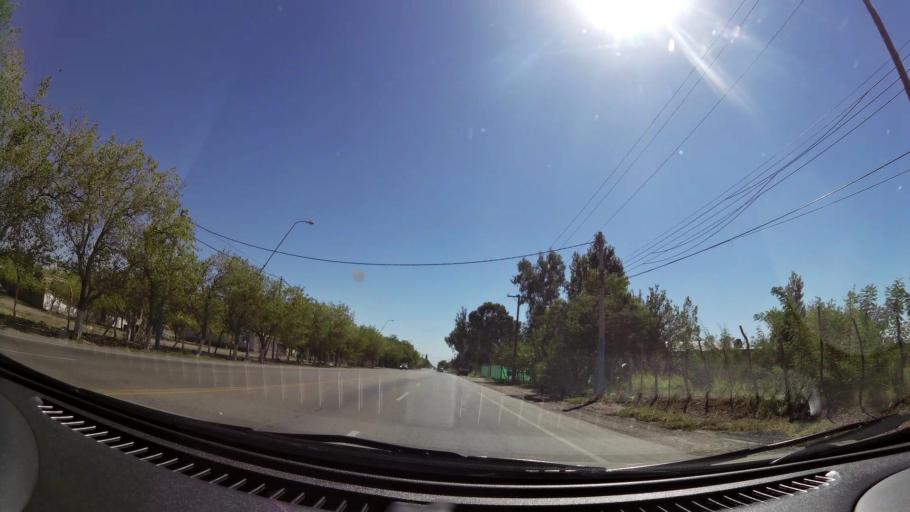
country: AR
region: San Juan
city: Villa Krause
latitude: -31.6049
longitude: -68.5437
